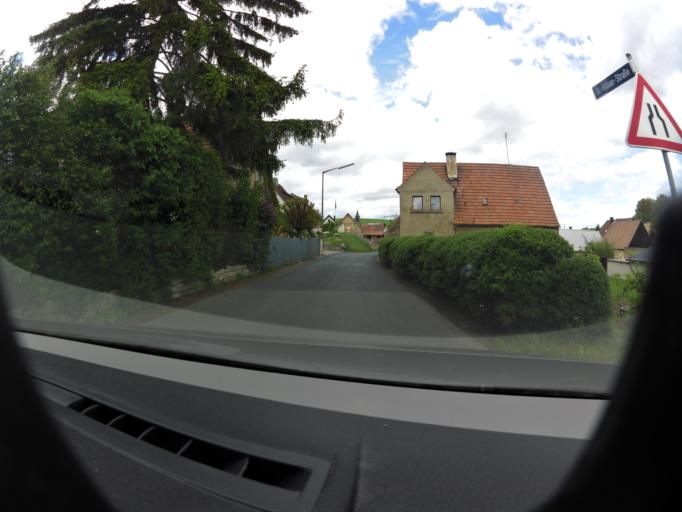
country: DE
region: Bavaria
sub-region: Regierungsbezirk Unterfranken
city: Dettelbach
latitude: 49.8294
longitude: 10.1494
